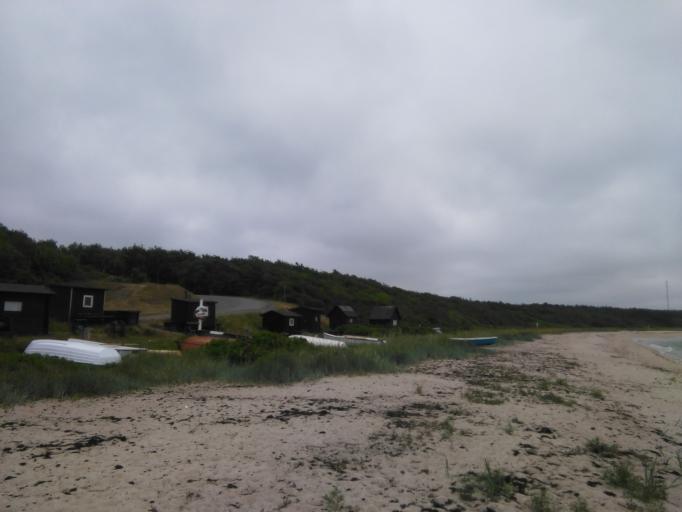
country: DK
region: Capital Region
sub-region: Bornholm Kommune
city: Ronne
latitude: 55.1480
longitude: 14.7045
